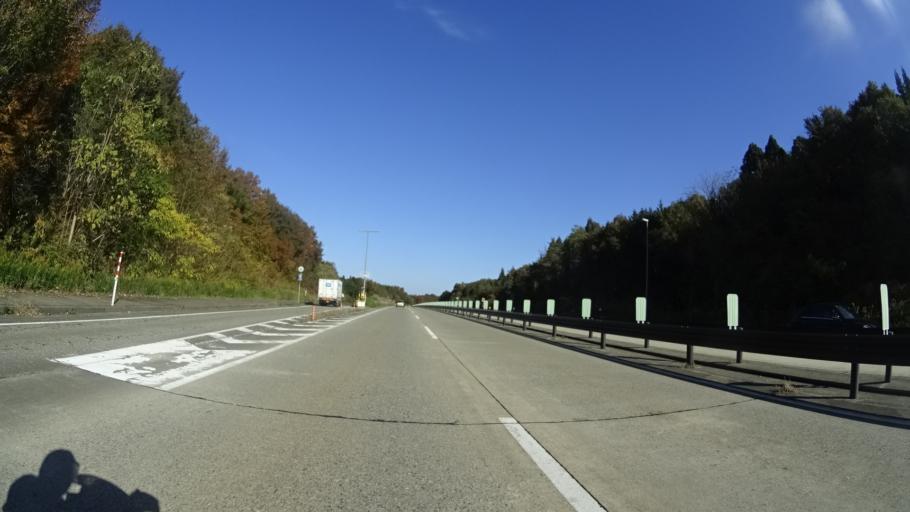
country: JP
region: Ishikawa
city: Komatsu
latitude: 36.3527
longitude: 136.4515
